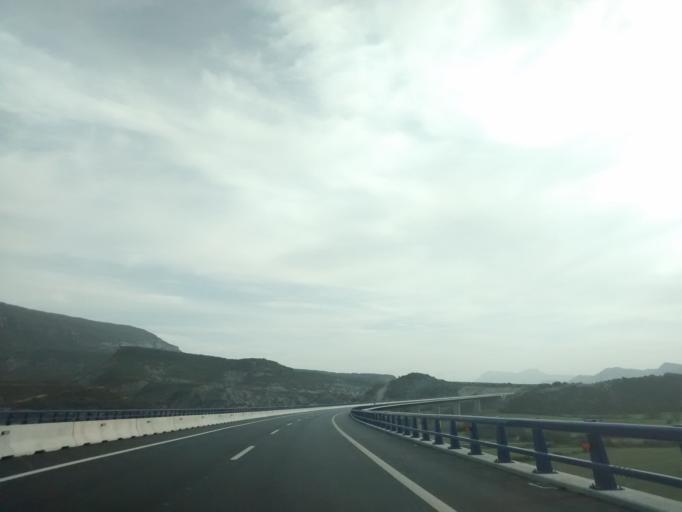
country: ES
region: Aragon
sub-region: Provincia de Zaragoza
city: Siguees
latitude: 42.6260
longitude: -1.0191
